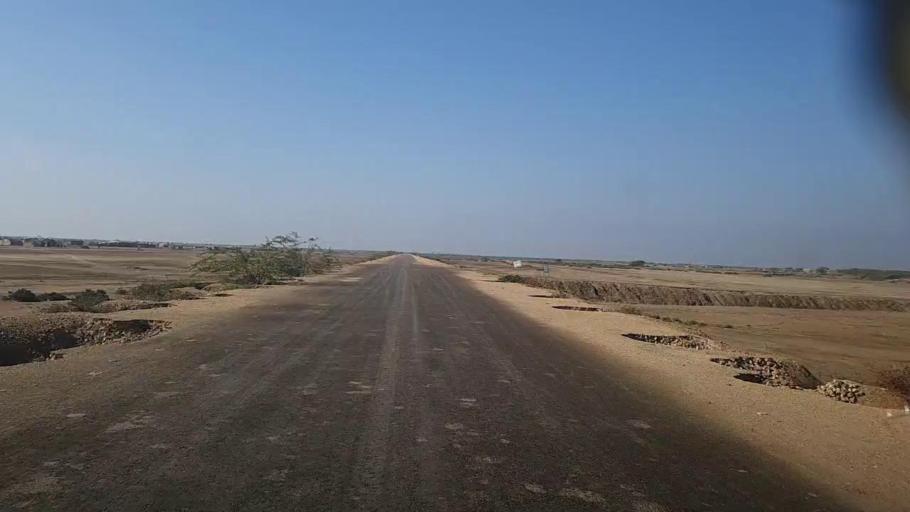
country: PK
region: Sindh
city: Mirpur Sakro
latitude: 24.5551
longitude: 67.4927
